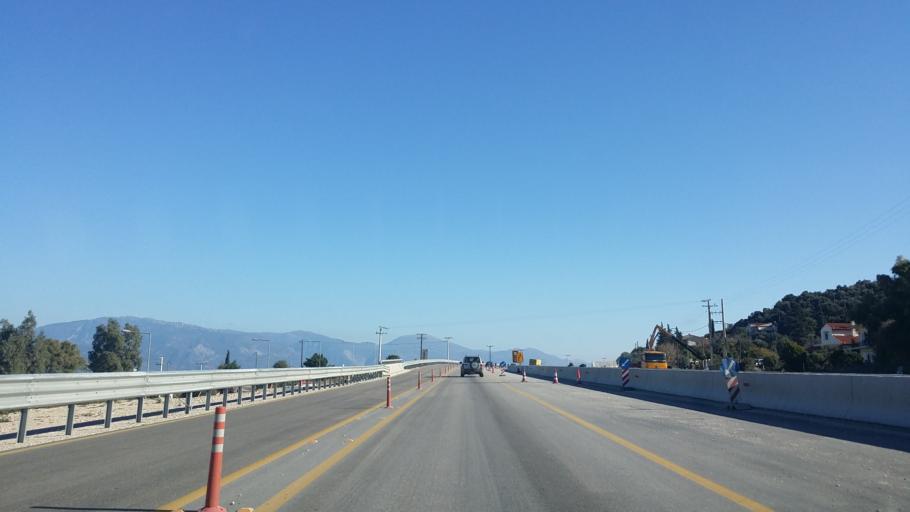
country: GR
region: West Greece
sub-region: Nomos Achaias
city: Ano Kastritsion
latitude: 38.3240
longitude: 21.8910
